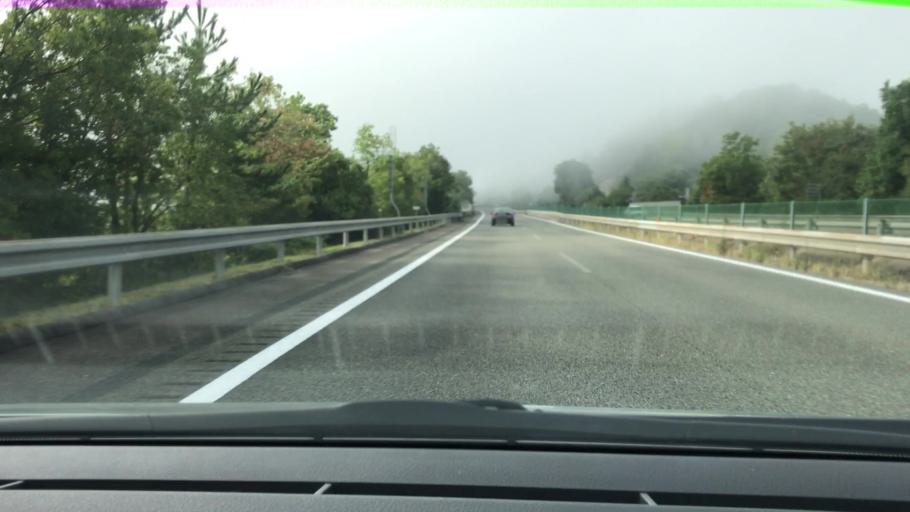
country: JP
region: Hyogo
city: Sasayama
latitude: 35.0993
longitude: 135.1699
